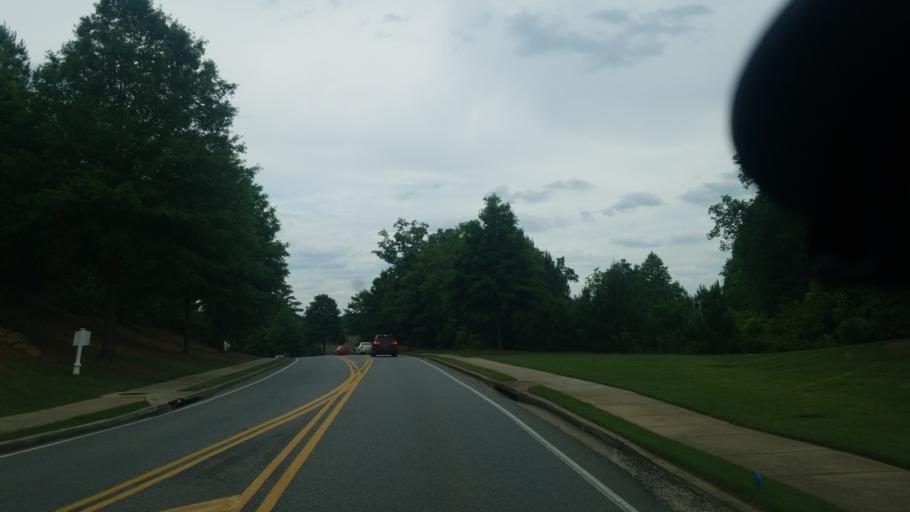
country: US
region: Georgia
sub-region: Forsyth County
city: Cumming
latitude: 34.1328
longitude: -84.1390
